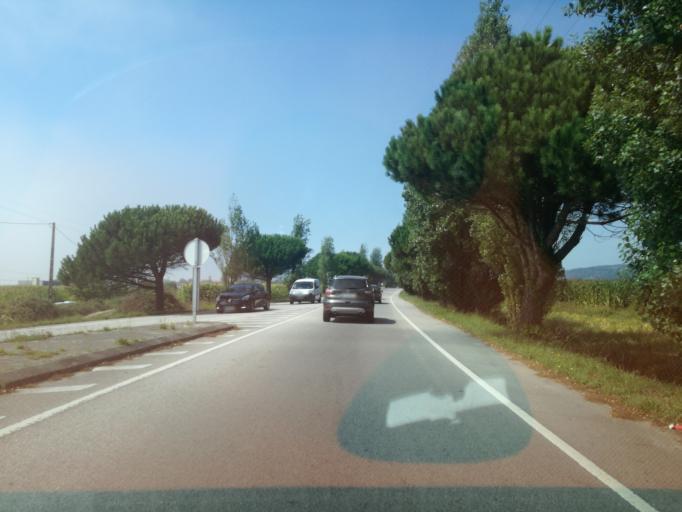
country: PT
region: Braga
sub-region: Esposende
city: Esposende
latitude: 41.5206
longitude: -8.7710
